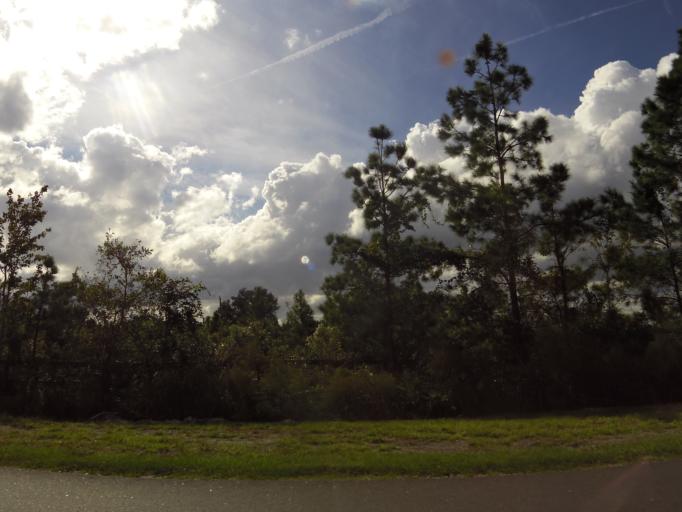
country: US
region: Florida
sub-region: Saint Johns County
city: Villano Beach
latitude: 29.9981
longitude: -81.3954
